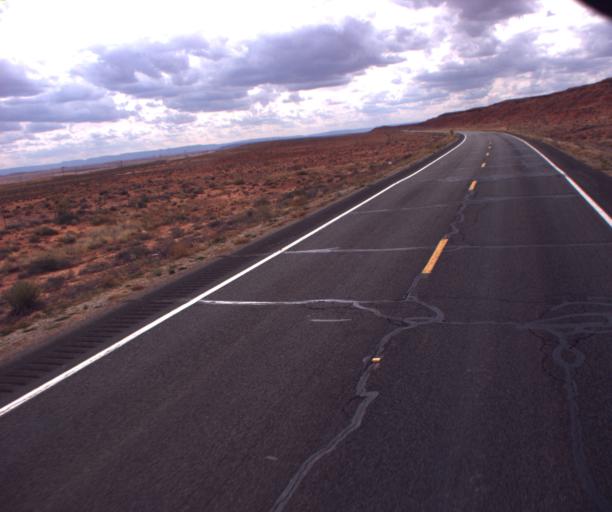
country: US
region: Arizona
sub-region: Navajo County
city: Kayenta
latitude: 36.9126
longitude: -109.7789
